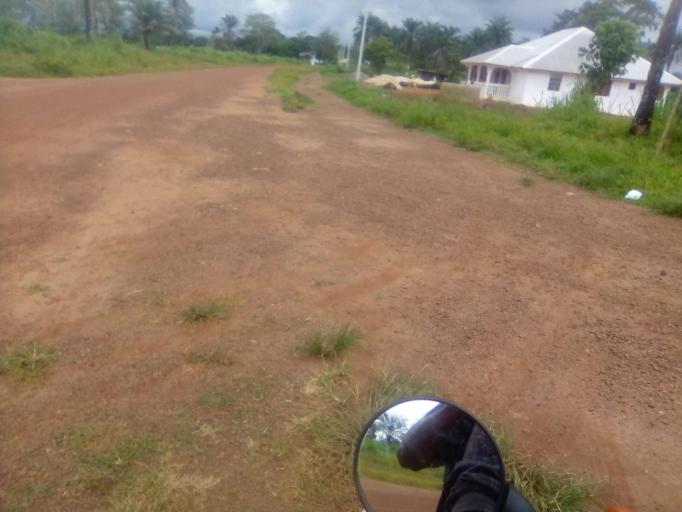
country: SL
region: Southern Province
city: Moyamba
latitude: 8.1464
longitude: -12.4385
